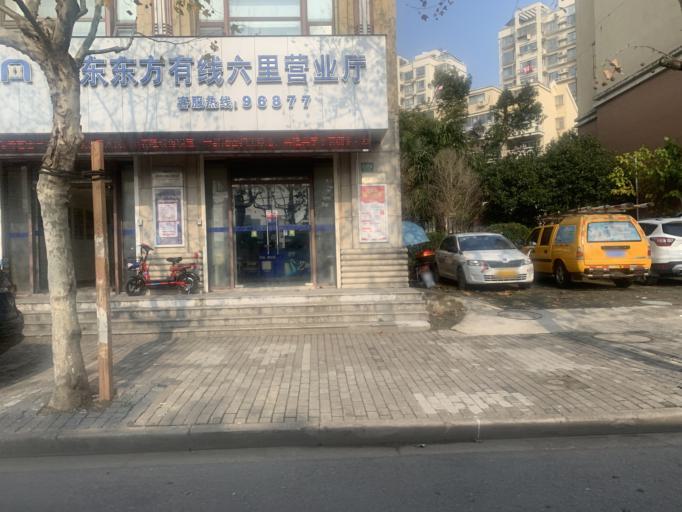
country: CN
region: Shanghai Shi
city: Huamu
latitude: 31.1832
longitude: 121.5233
